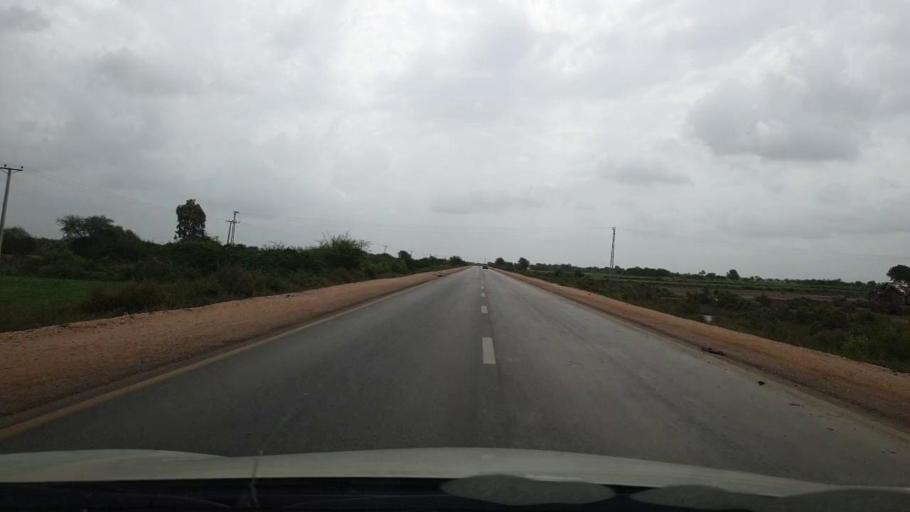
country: PK
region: Sindh
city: Mirpur Batoro
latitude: 24.6231
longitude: 68.3259
